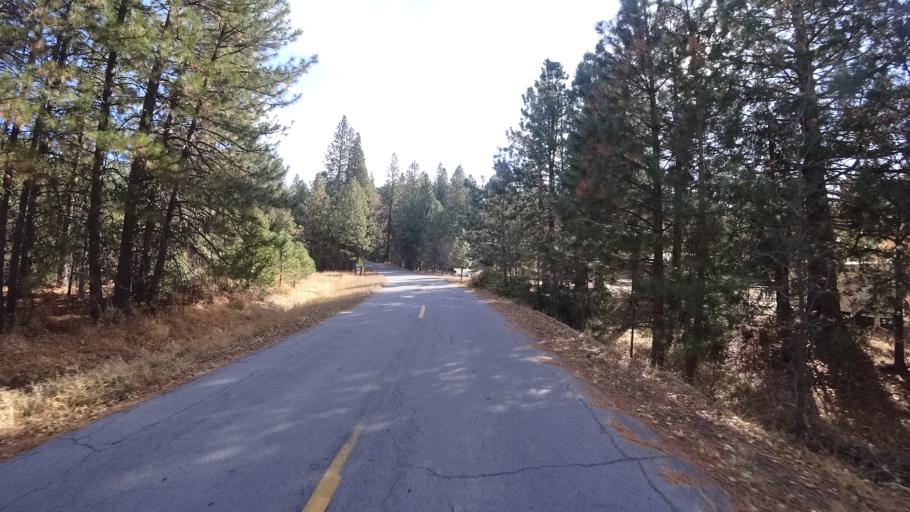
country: US
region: California
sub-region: Siskiyou County
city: Weed
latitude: 41.4315
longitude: -122.4137
